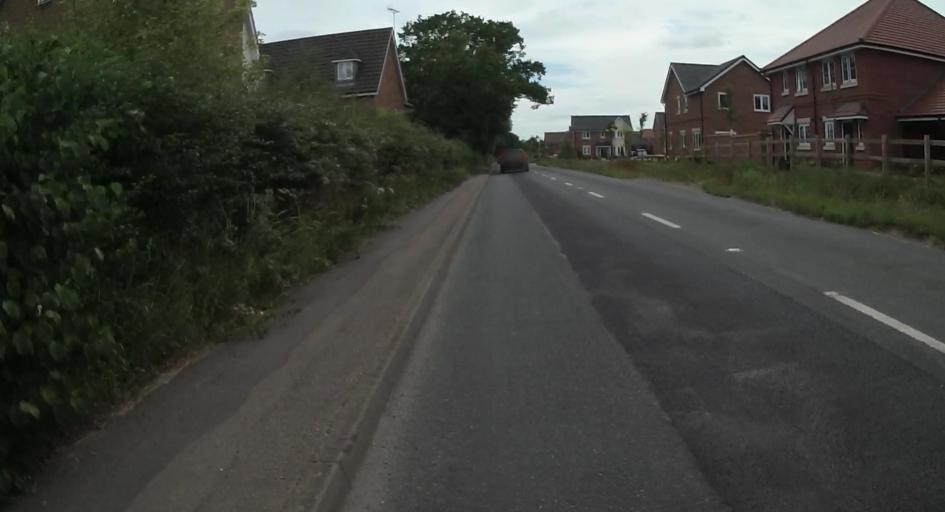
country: GB
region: England
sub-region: Wokingham
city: Swallowfield
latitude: 51.3891
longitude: -0.9772
